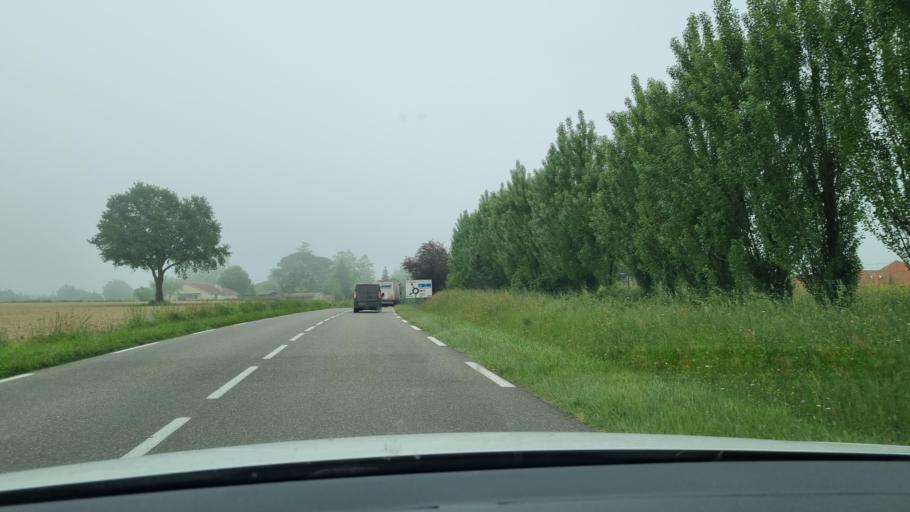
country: FR
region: Aquitaine
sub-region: Departement des Landes
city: Hagetmau
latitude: 43.6671
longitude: -0.5942
